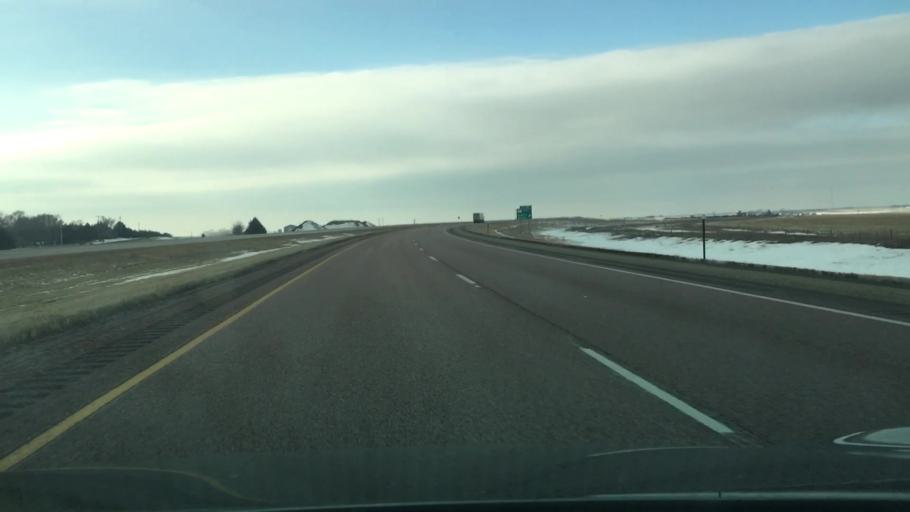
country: US
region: South Dakota
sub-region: Brule County
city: Chamberlain
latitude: 43.8467
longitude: -99.5554
